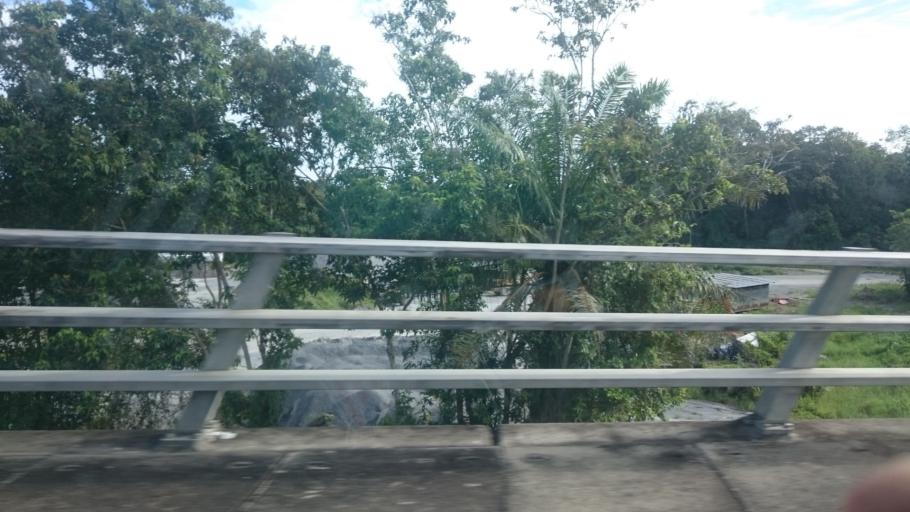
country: MY
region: Sarawak
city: Limbang
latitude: 4.6567
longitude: 114.8295
